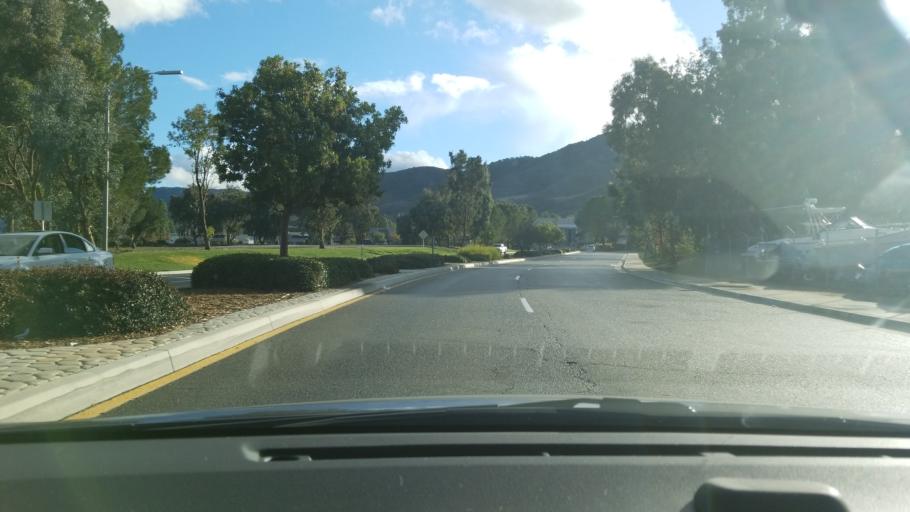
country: US
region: California
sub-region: Riverside County
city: Temecula
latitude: 33.5005
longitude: -117.1566
